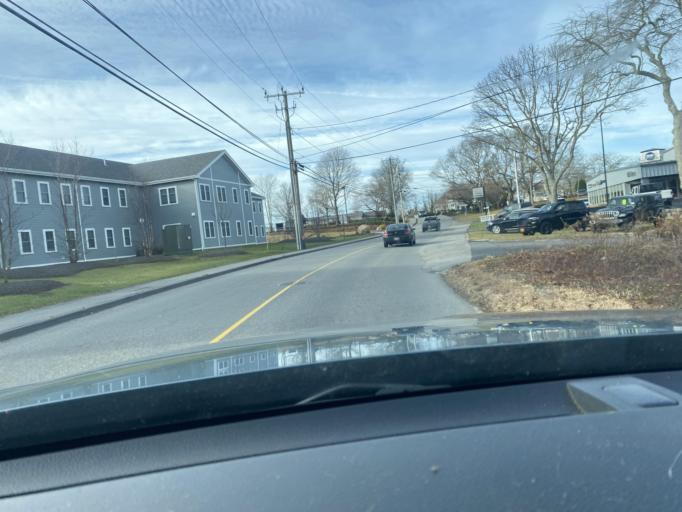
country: US
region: Massachusetts
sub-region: Barnstable County
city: Teaticket
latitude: 41.5582
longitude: -70.5954
